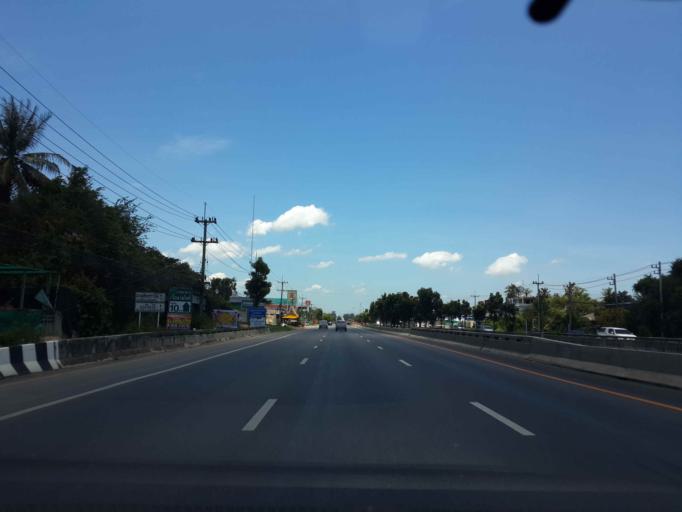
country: TH
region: Phetchaburi
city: Tha Yang
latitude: 12.9901
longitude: 99.9031
